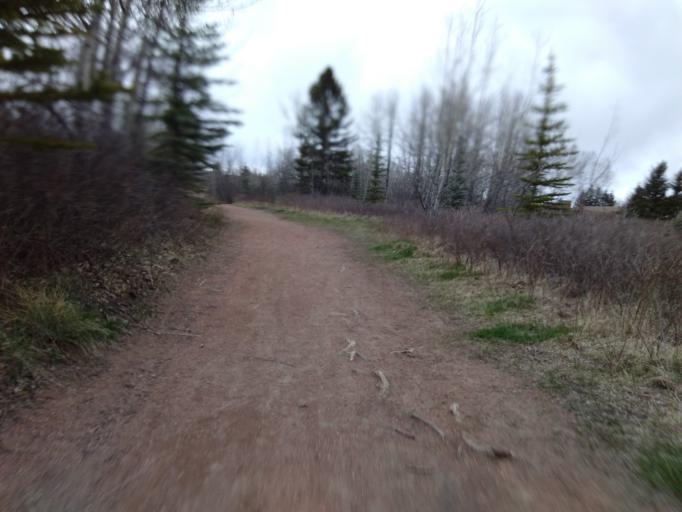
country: CA
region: Alberta
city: Cochrane
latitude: 51.1845
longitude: -114.4819
